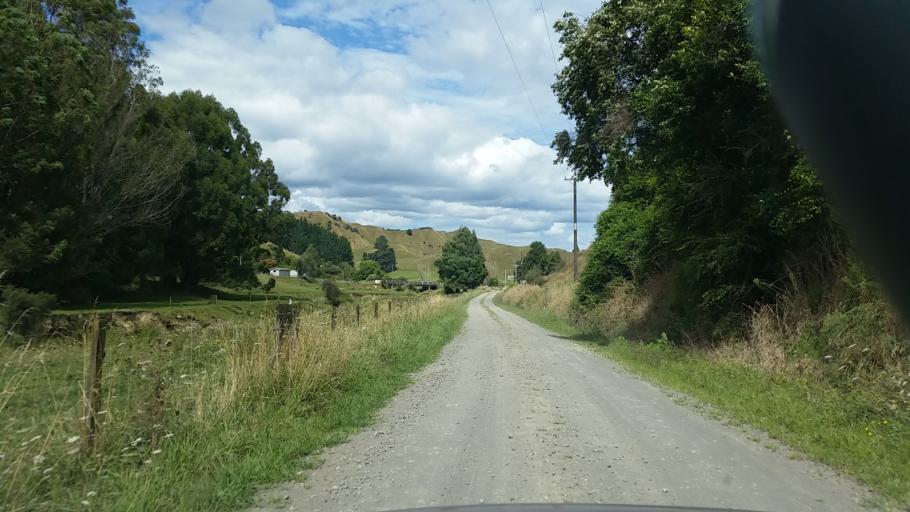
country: NZ
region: Taranaki
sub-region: South Taranaki District
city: Eltham
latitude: -39.2597
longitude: 174.5659
